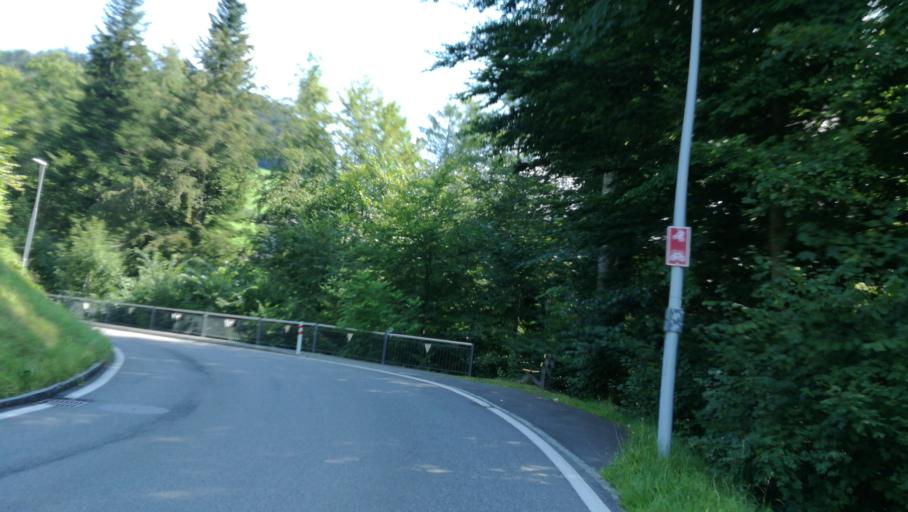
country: CH
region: Zug
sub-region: Zug
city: Unterageri
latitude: 47.1415
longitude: 8.5842
